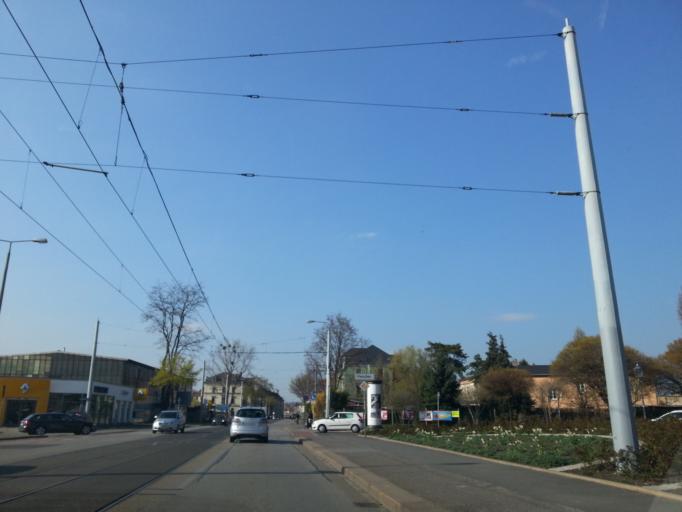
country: DE
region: Saxony
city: Dresden
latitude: 51.0726
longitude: 13.7359
